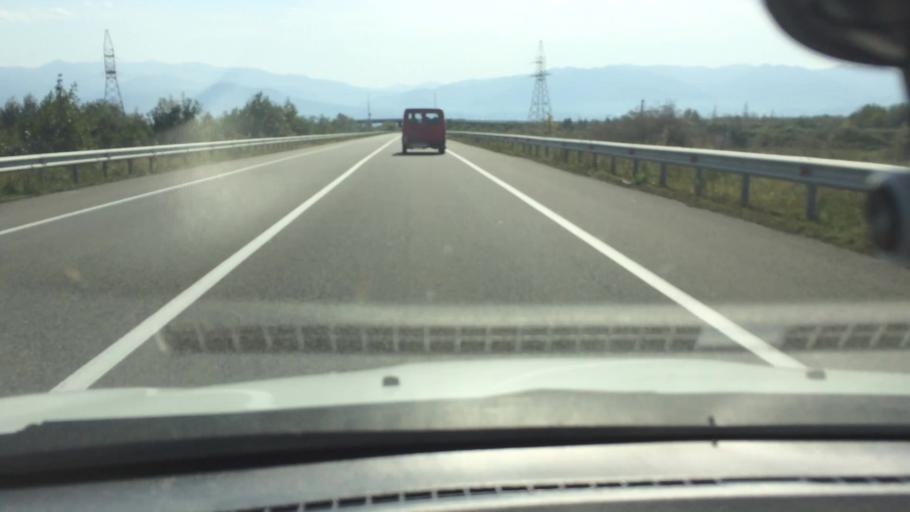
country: GE
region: Ajaria
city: Ochkhamuri
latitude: 41.9021
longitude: 41.7929
